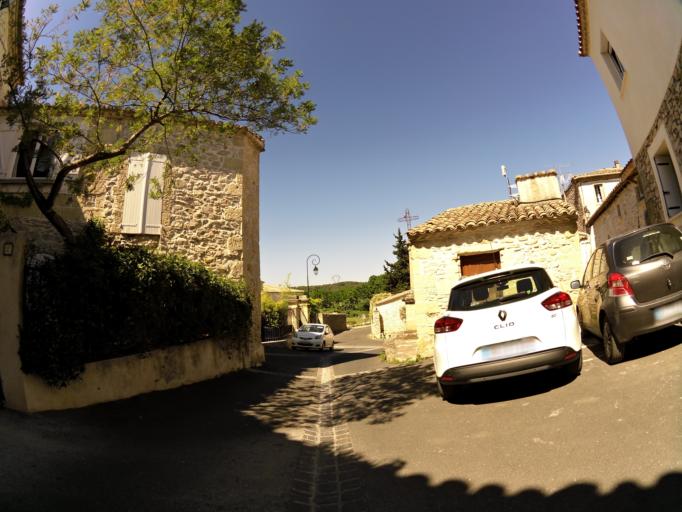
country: FR
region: Languedoc-Roussillon
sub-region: Departement de l'Herault
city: Villetelle
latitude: 43.7346
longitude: 4.1397
